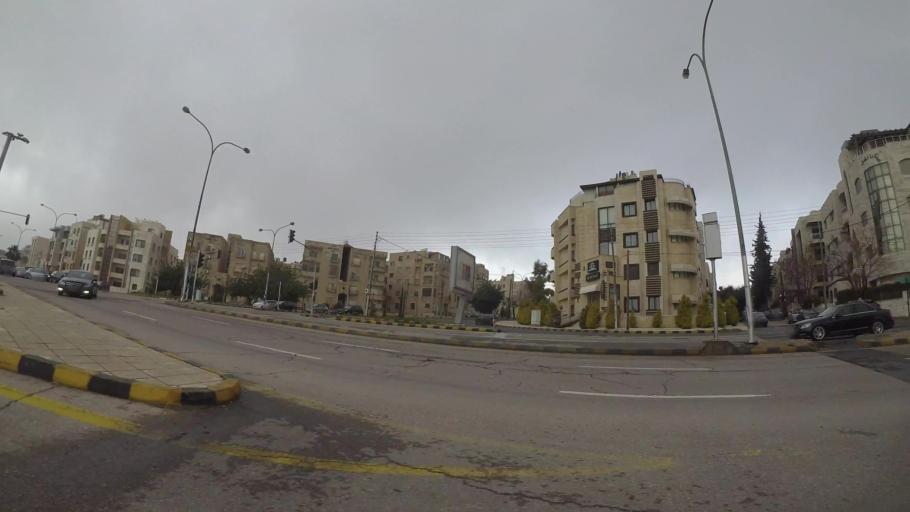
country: JO
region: Amman
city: Wadi as Sir
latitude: 31.9465
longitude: 35.8706
